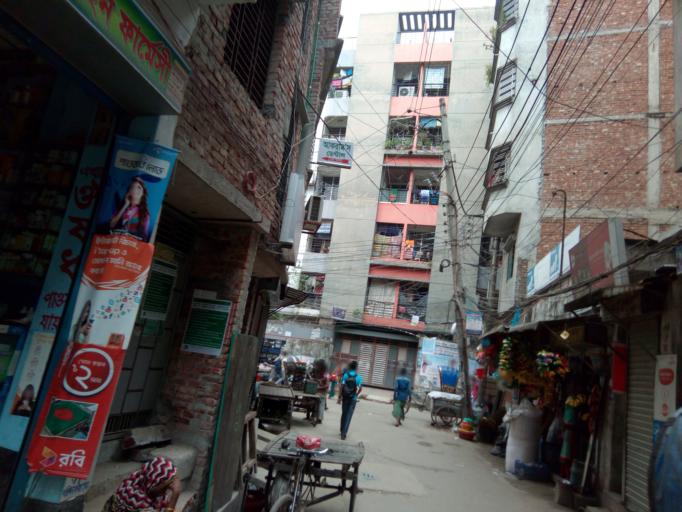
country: BD
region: Dhaka
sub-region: Dhaka
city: Dhaka
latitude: 23.7213
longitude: 90.4017
